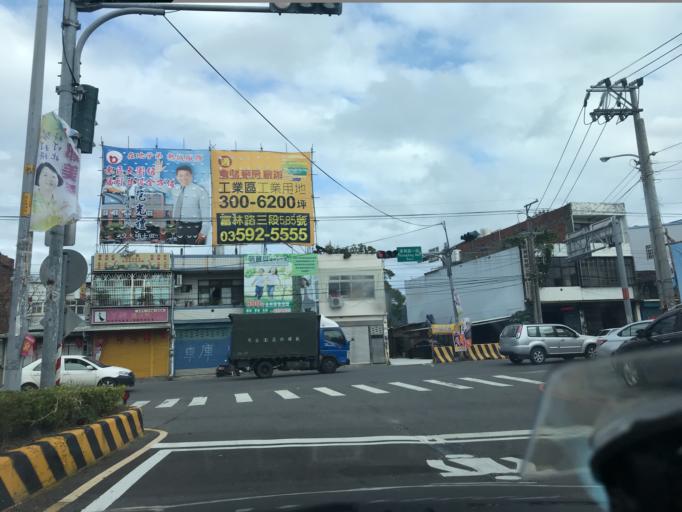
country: TW
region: Taiwan
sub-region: Hsinchu
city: Zhubei
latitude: 24.8040
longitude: 121.0497
